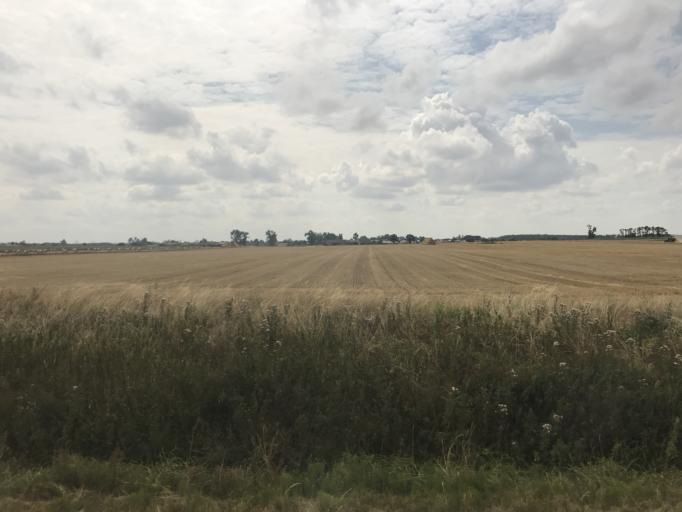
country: PL
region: Greater Poland Voivodeship
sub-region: Powiat gnieznienski
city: Gniezno
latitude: 52.5150
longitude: 17.5317
